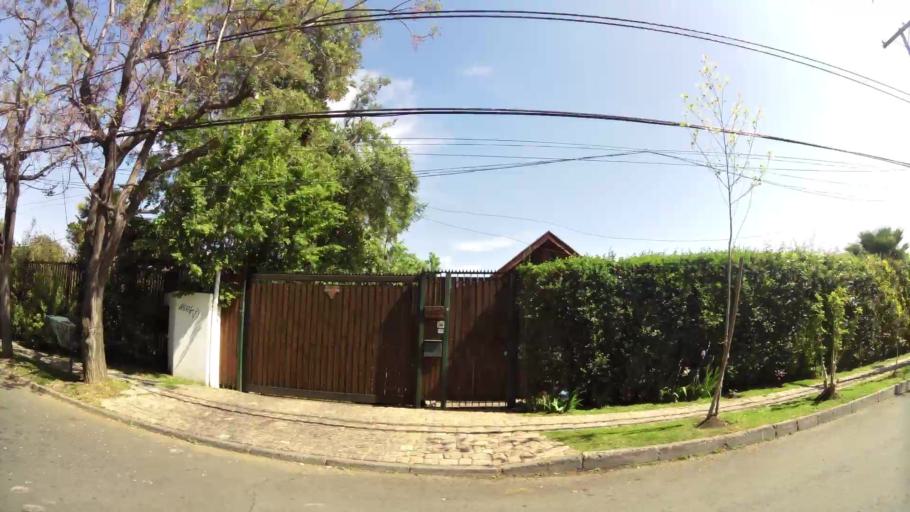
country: CL
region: Santiago Metropolitan
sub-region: Provincia de Santiago
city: Villa Presidente Frei, Nunoa, Santiago, Chile
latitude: -33.4541
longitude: -70.5248
